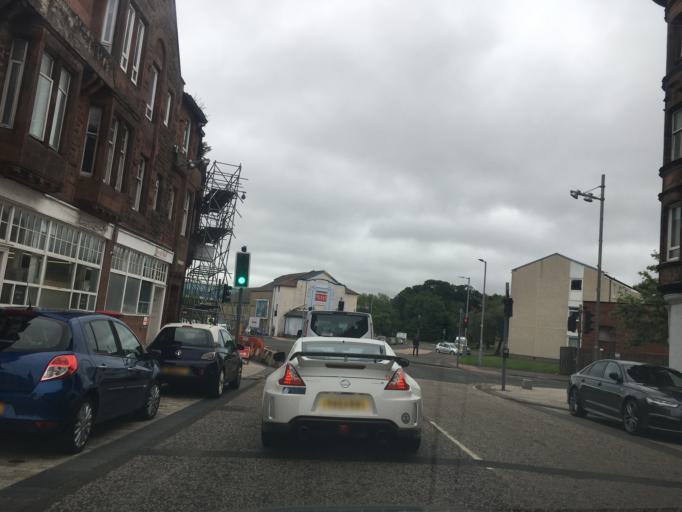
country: GB
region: Scotland
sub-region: Renfrewshire
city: Renfrew
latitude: 55.8796
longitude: -4.3857
